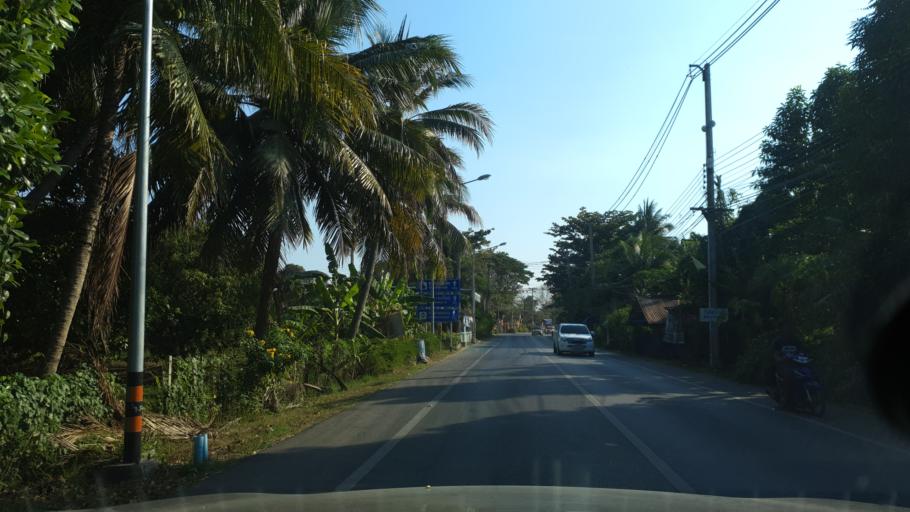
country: TH
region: Samut Songkhram
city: Bang Khon Thi
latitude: 13.4476
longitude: 99.9417
